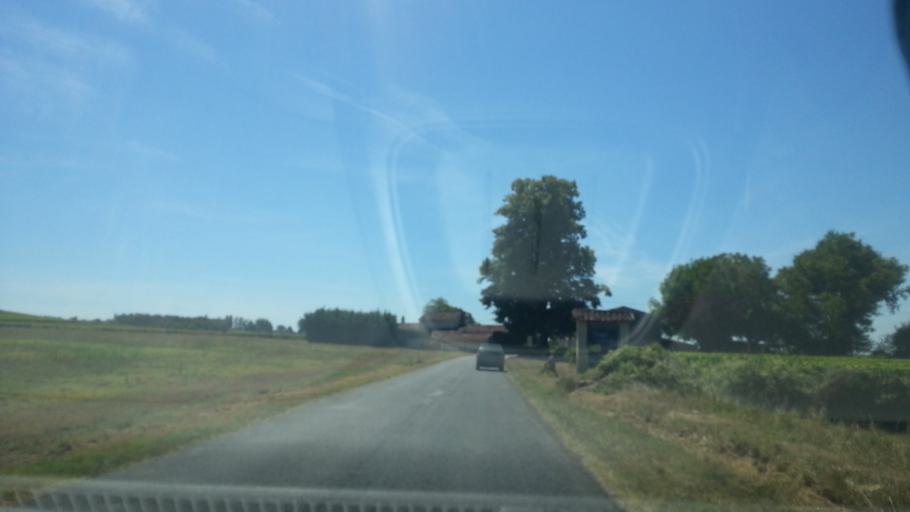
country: FR
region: Aquitaine
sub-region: Departement de la Gironde
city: Illats
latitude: 44.5535
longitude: -0.3508
